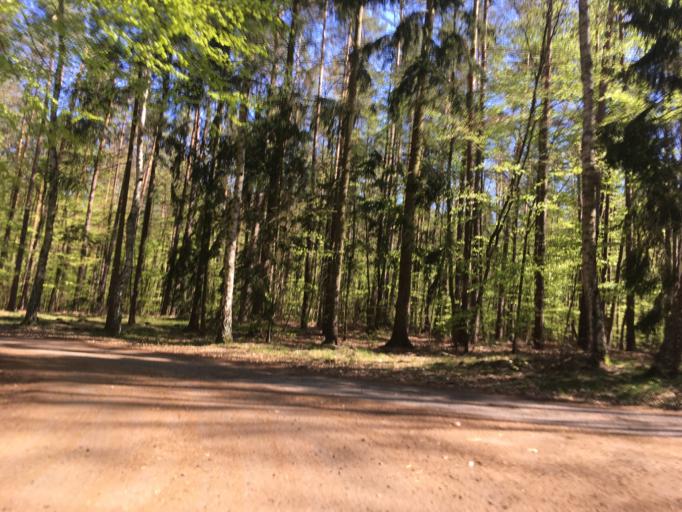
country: DE
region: Brandenburg
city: Wandlitz
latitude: 52.7497
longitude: 13.5364
